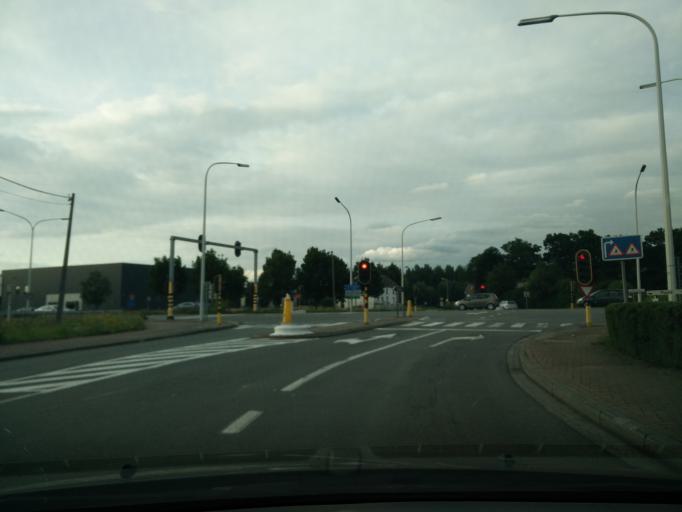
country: BE
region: Flanders
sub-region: Provincie Antwerpen
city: Puurs
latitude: 51.0885
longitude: 4.2752
